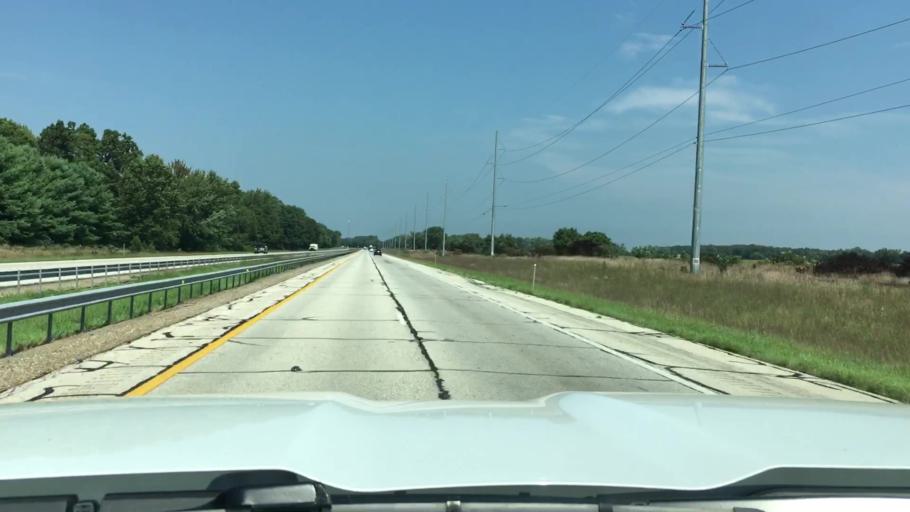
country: US
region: Michigan
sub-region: Saint Joseph County
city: Three Rivers
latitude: 42.0016
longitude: -85.6334
